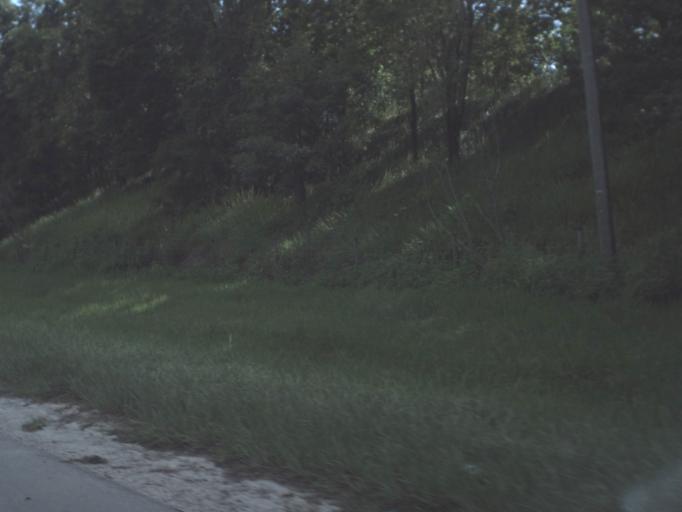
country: US
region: Florida
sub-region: Hernando County
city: North Brooksville
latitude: 28.5733
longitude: -82.4210
